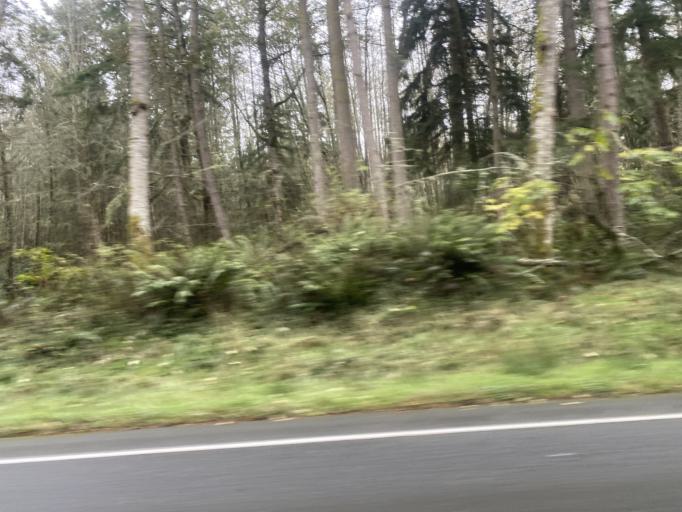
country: US
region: Washington
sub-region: Island County
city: Freeland
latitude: 48.0482
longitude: -122.5068
